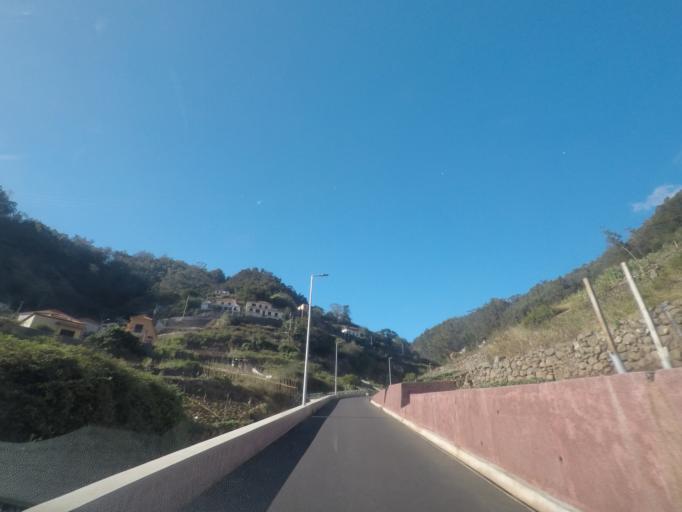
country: PT
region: Madeira
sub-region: Ribeira Brava
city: Campanario
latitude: 32.6653
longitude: -17.0058
